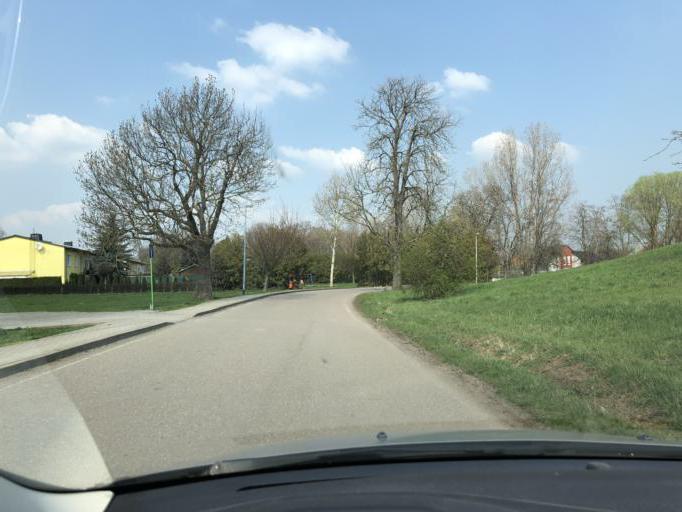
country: DE
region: Saxony-Anhalt
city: Landsberg
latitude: 51.5415
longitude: 12.1348
